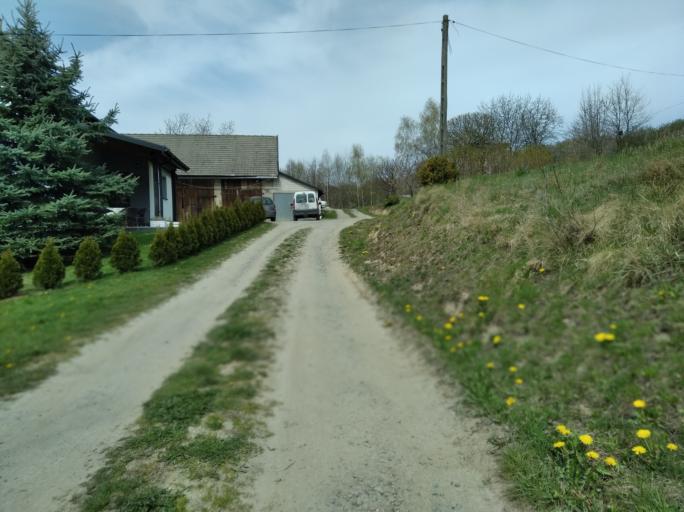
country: PL
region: Subcarpathian Voivodeship
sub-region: Powiat ropczycko-sedziszowski
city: Wielopole Skrzynskie
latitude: 49.9096
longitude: 21.6135
